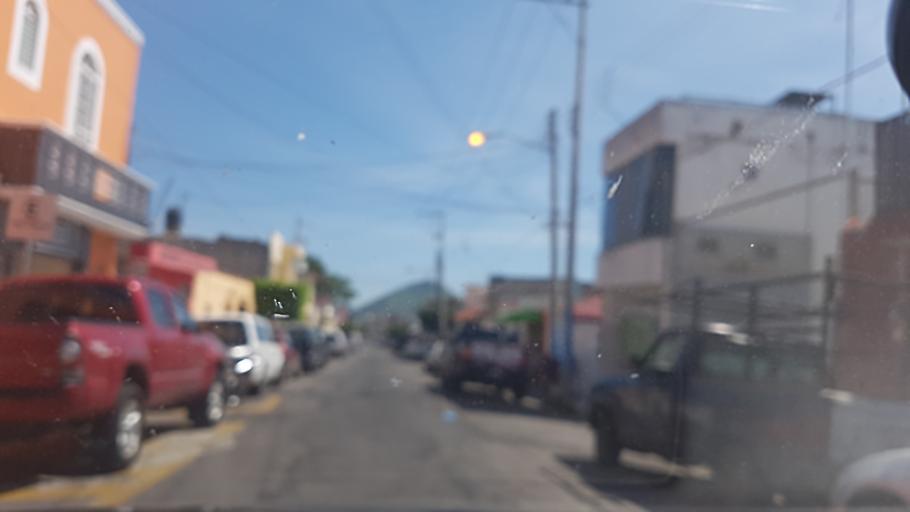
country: MX
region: Nayarit
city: Tepic
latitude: 21.5067
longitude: -104.8997
